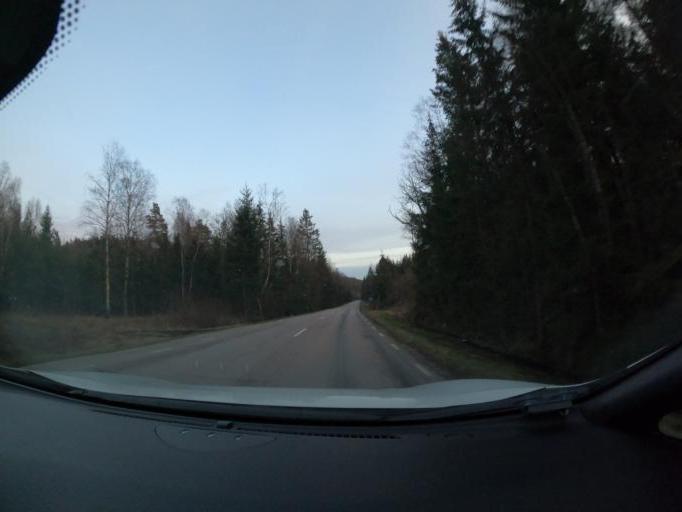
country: SE
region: Vaestra Goetaland
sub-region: Harryda Kommun
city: Landvetter
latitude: 57.6302
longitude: 12.1794
